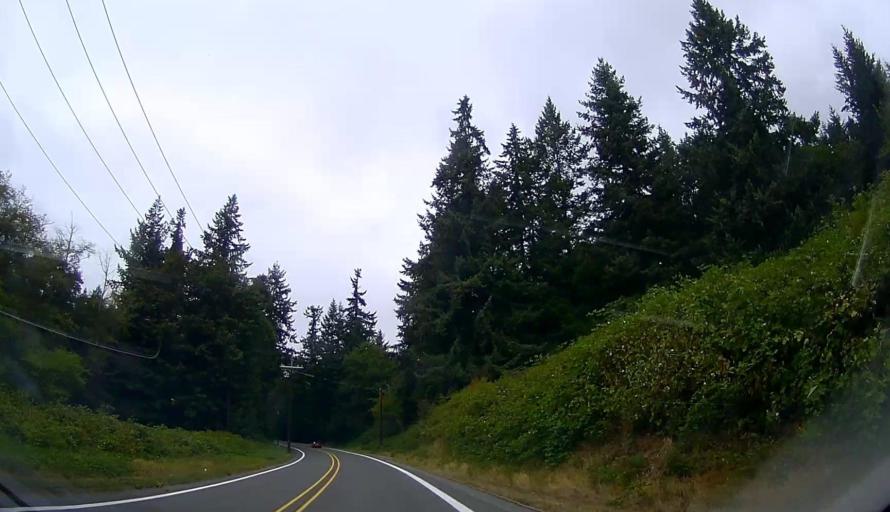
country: US
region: Washington
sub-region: Snohomish County
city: Warm Beach
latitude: 48.1428
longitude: -122.3575
